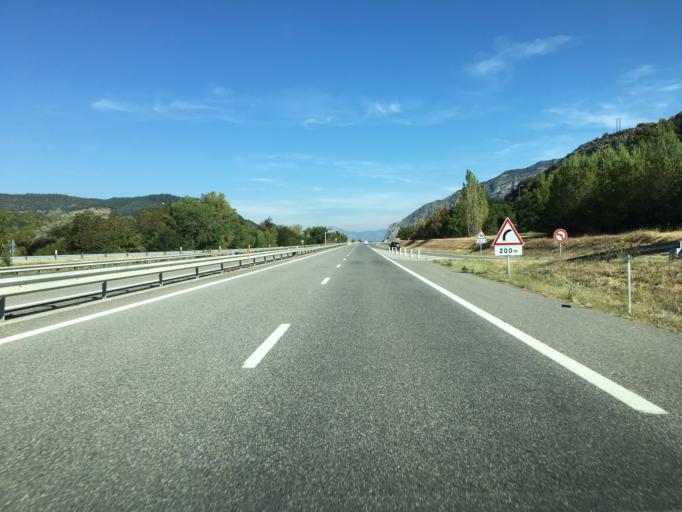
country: FR
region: Provence-Alpes-Cote d'Azur
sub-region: Departement des Alpes-de-Haute-Provence
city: Sisteron
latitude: 44.1701
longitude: 5.9550
